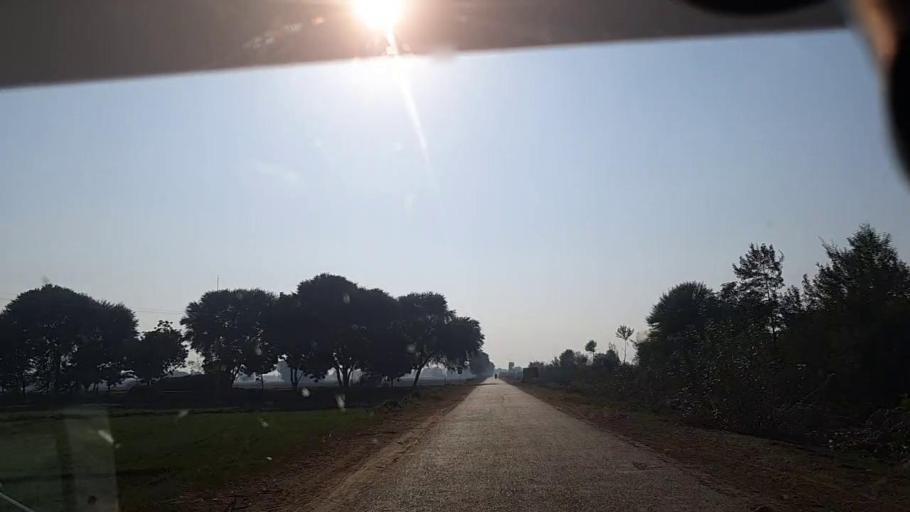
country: PK
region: Sindh
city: Sobhadero
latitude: 27.2457
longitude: 68.2906
